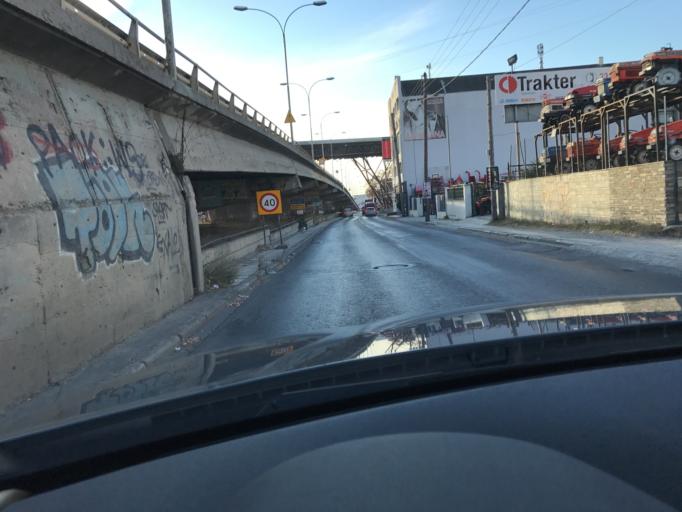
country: GR
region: Central Macedonia
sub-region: Nomos Thessalonikis
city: Stavroupoli
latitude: 40.6784
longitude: 22.9387
